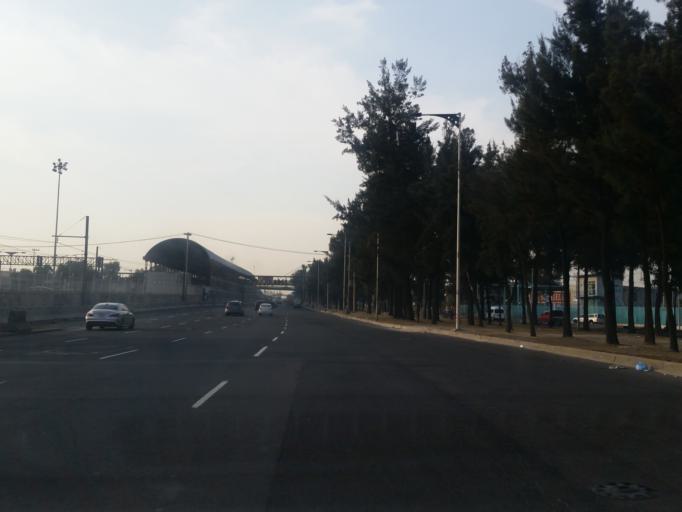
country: MX
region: Mexico
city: Los Reyes La Paz
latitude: 19.3635
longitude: -99.0038
